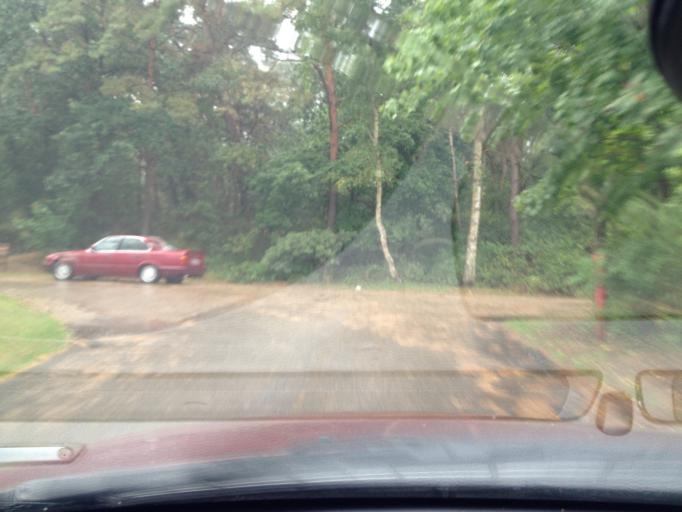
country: PL
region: West Pomeranian Voivodeship
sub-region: Powiat gryficki
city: Pobierowo
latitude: 54.0566
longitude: 14.9122
